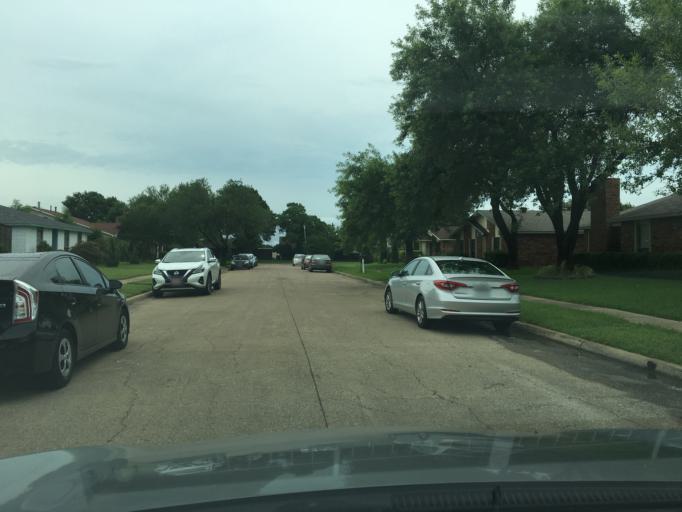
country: US
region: Texas
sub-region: Dallas County
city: Richardson
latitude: 32.9531
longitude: -96.6821
